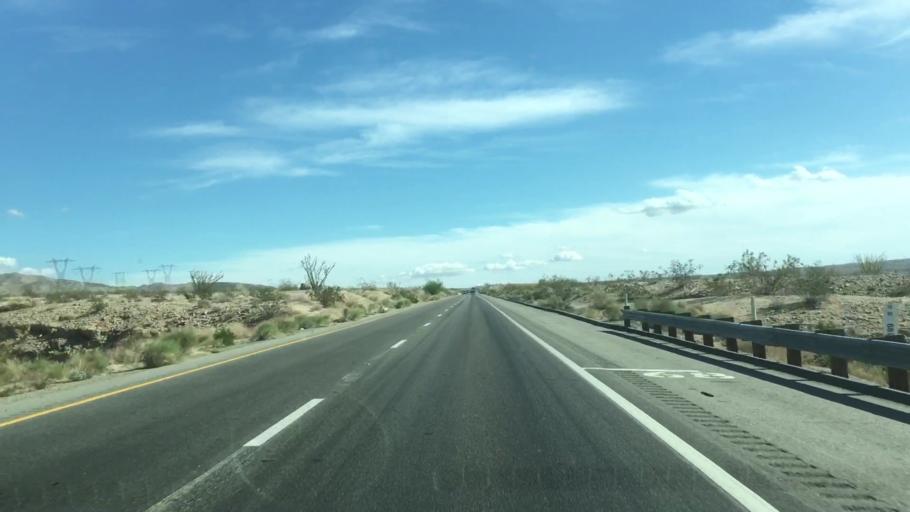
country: US
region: California
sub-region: Riverside County
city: Thermal
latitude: 33.6878
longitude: -116.0339
